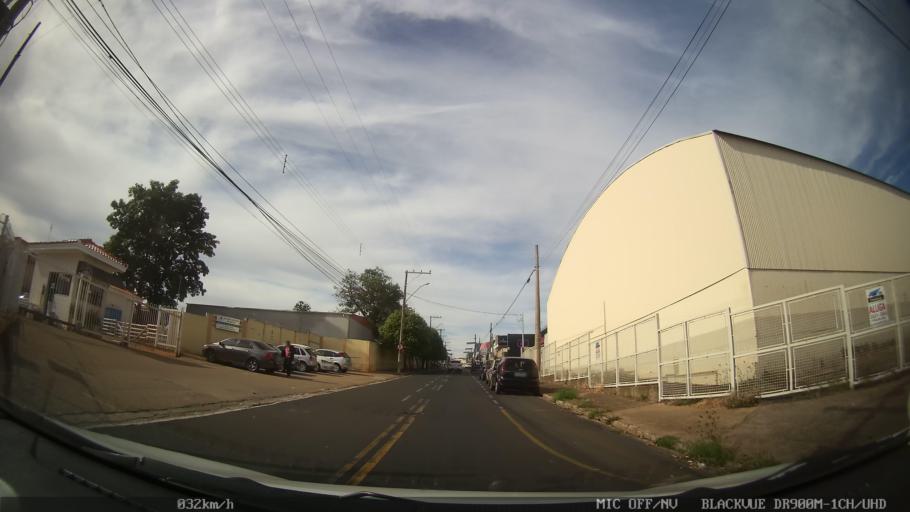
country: BR
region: Sao Paulo
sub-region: Catanduva
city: Catanduva
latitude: -21.1434
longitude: -48.9678
